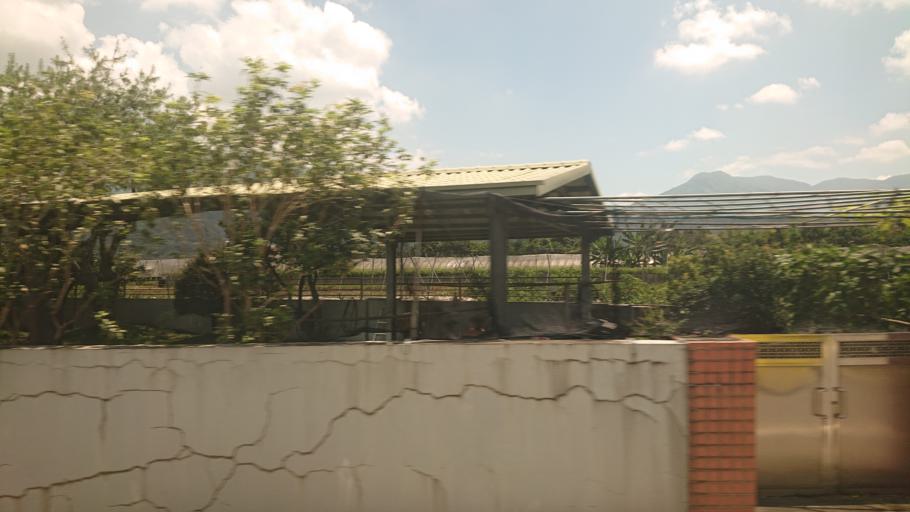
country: TW
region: Taiwan
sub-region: Nantou
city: Puli
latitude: 23.9813
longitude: 120.9603
